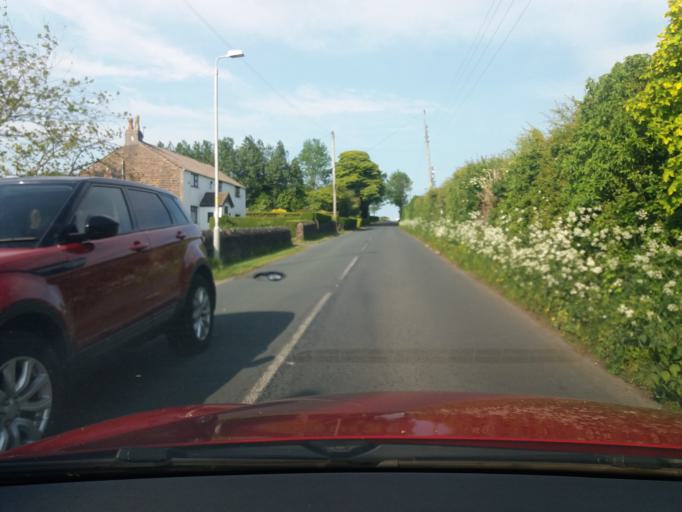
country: GB
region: England
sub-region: Lancashire
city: Chorley
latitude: 53.6858
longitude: -2.5850
